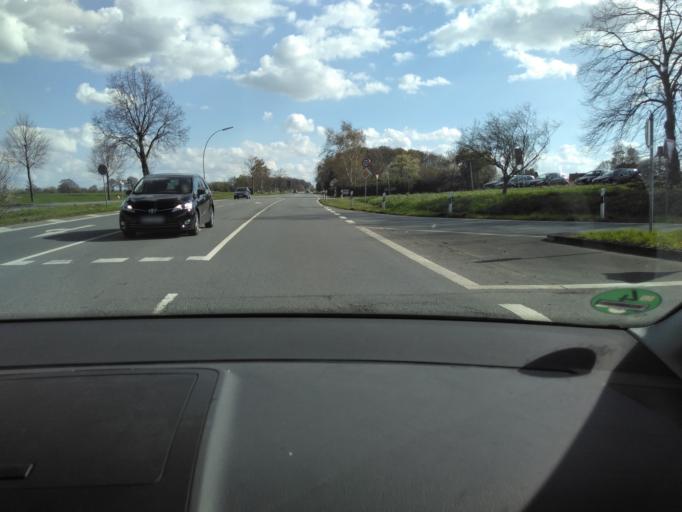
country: DE
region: North Rhine-Westphalia
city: Oelde
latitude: 51.8063
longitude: 8.1339
